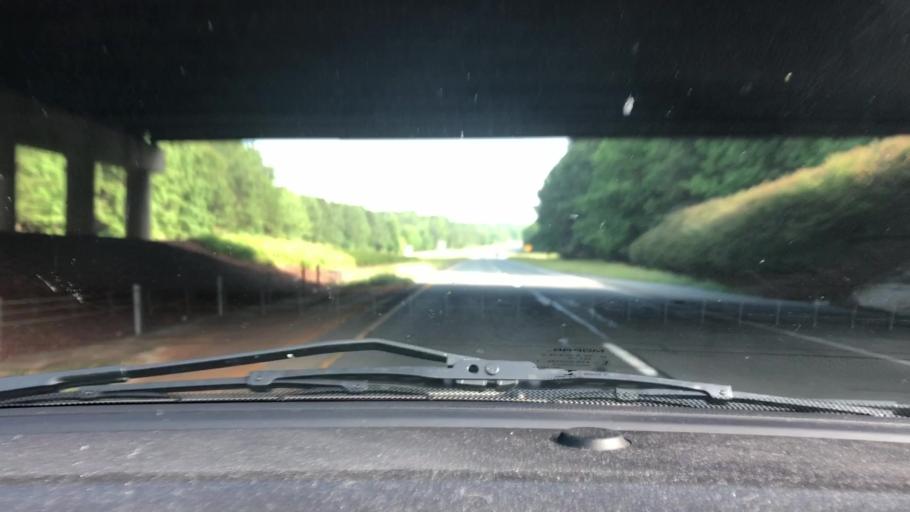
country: US
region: North Carolina
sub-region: Chatham County
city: Siler City
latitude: 35.7343
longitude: -79.4322
